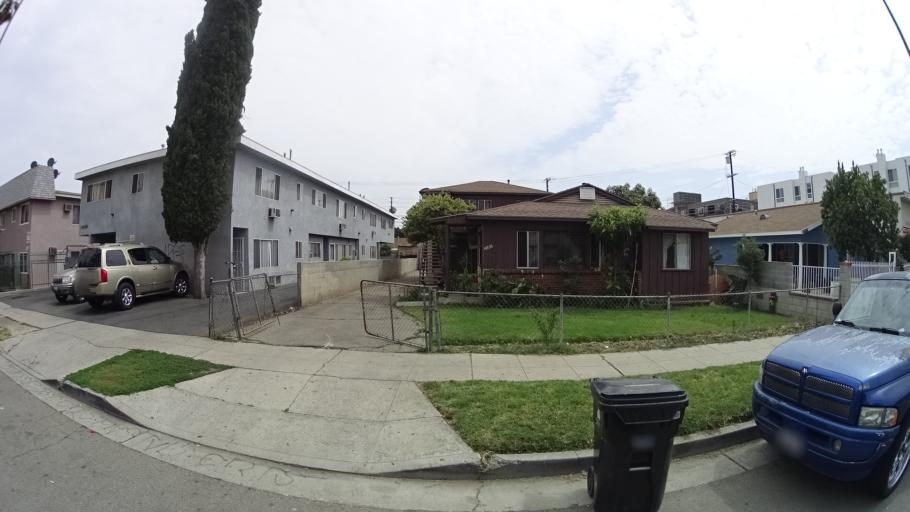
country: US
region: California
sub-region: Los Angeles County
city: Van Nuys
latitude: 34.1836
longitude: -118.4566
